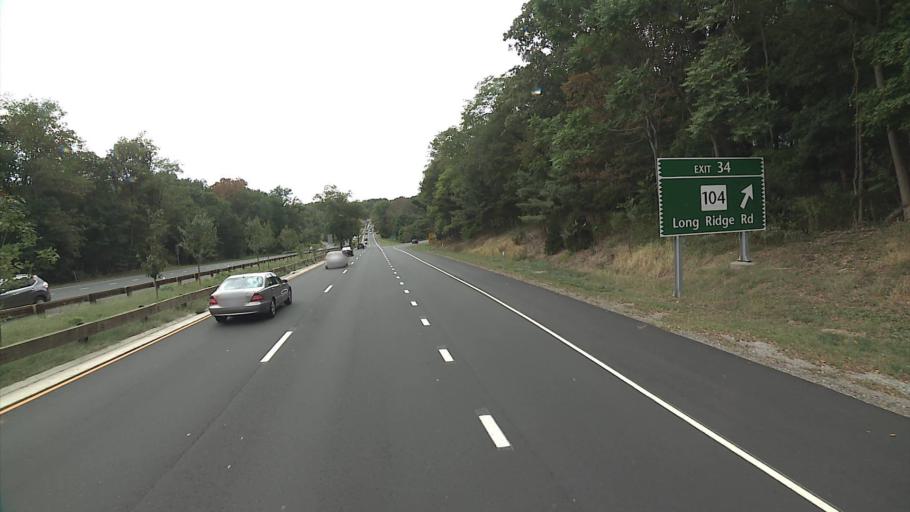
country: US
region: Connecticut
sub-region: Fairfield County
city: North Stamford
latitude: 41.1054
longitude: -73.5616
